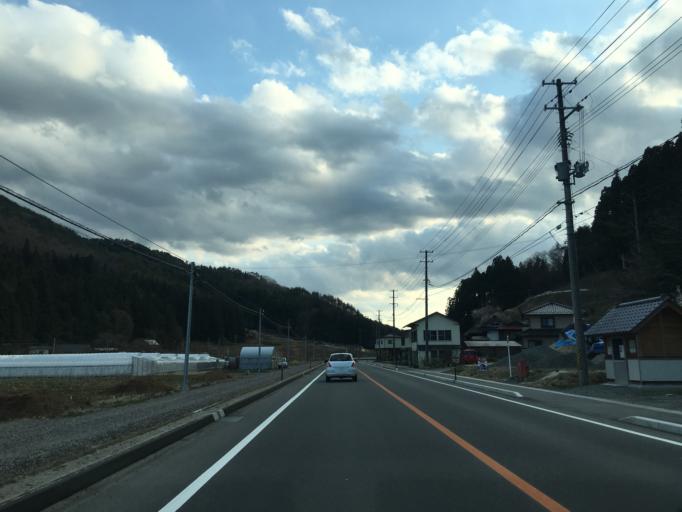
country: JP
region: Fukushima
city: Ishikawa
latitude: 37.0904
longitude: 140.5284
